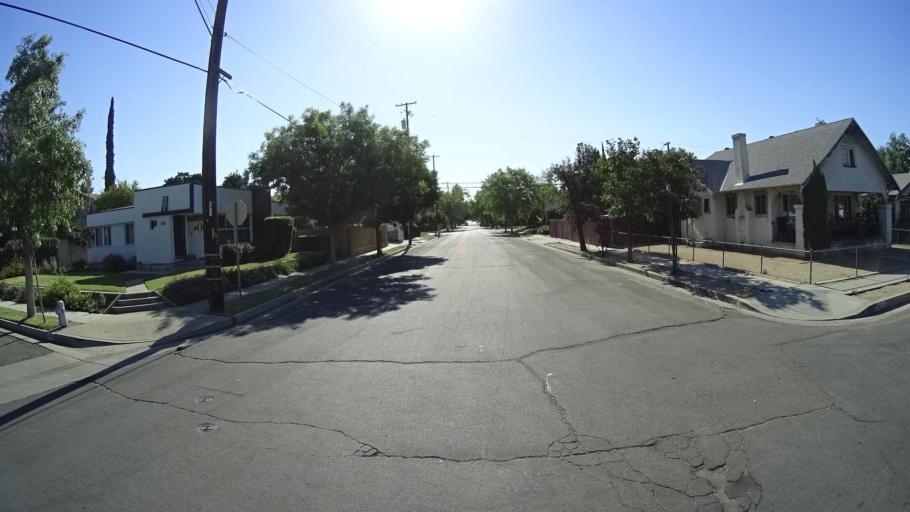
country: US
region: California
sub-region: Fresno County
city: Fresno
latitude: 36.7558
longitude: -119.8132
